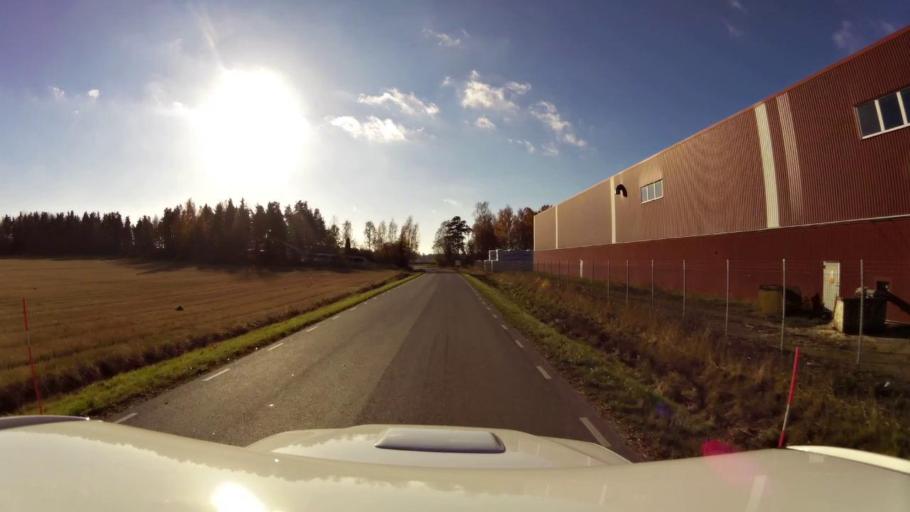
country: SE
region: OEstergoetland
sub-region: Linkopings Kommun
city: Linghem
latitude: 58.4396
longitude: 15.7777
